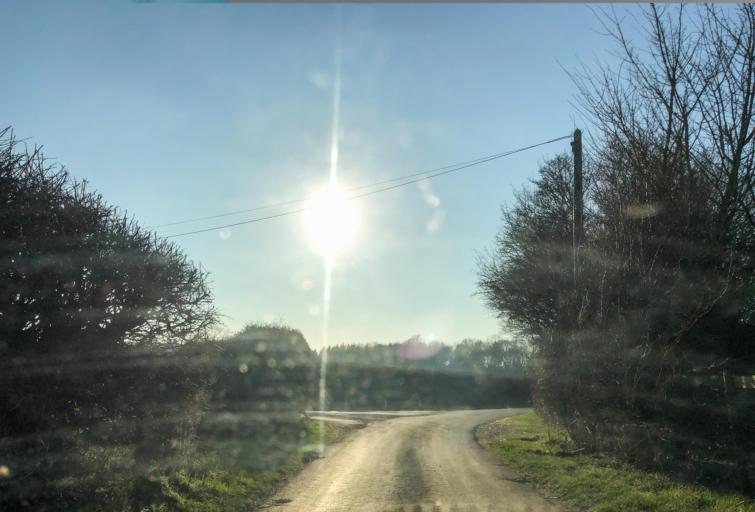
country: GB
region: England
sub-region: Warwickshire
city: Wellesbourne Mountford
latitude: 52.1992
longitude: -1.5232
